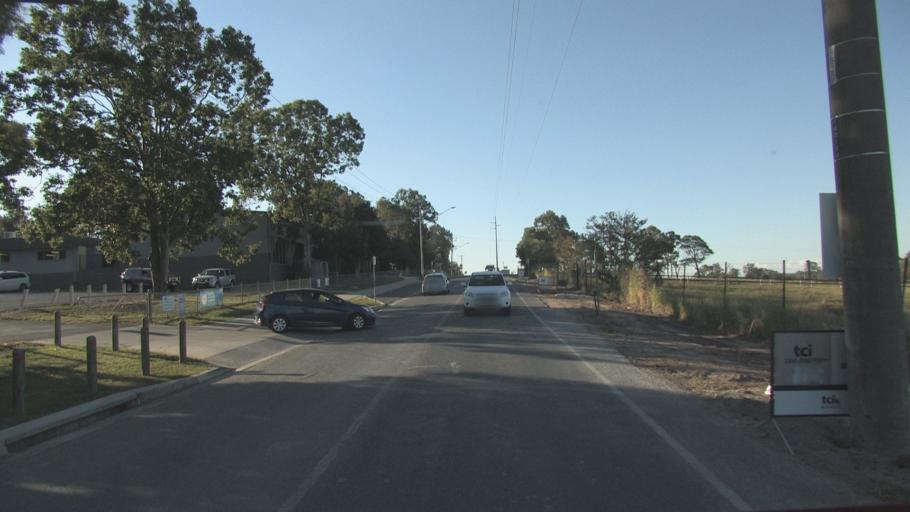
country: AU
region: Queensland
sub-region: Logan
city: Logan Reserve
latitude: -27.7156
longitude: 153.1155
